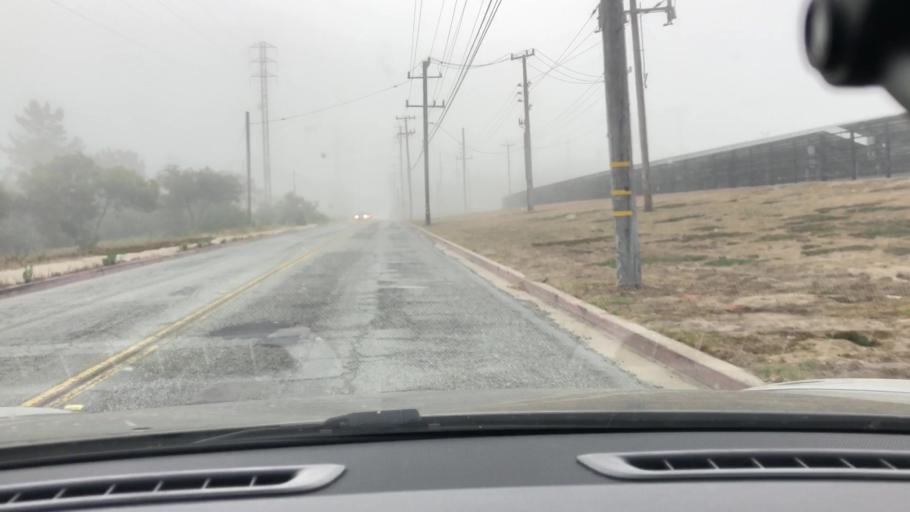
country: US
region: California
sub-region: Monterey County
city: Marina
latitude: 36.6438
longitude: -121.7951
